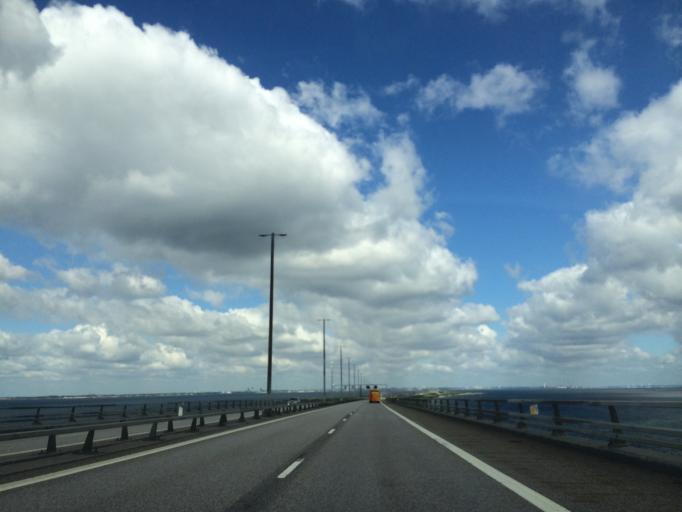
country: DK
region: Capital Region
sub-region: Dragor Kommune
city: Dragor
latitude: 55.5863
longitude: 12.7849
